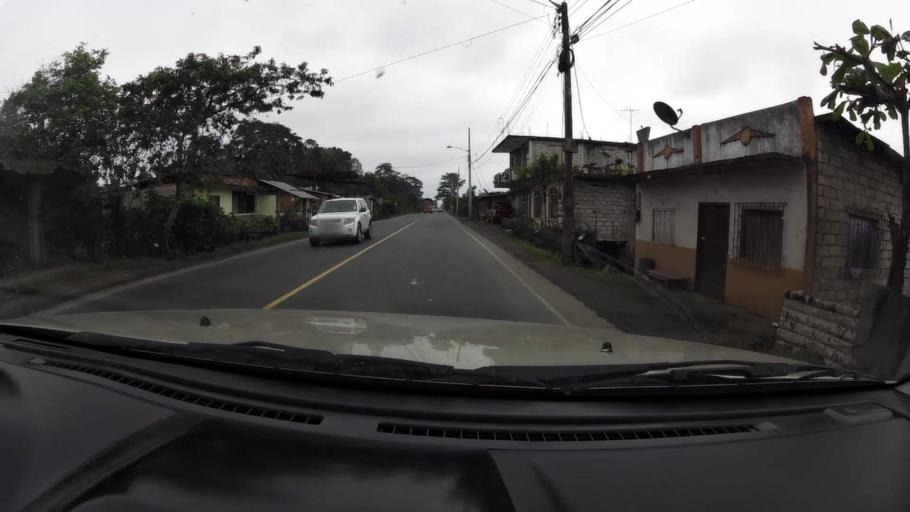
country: EC
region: Guayas
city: Balao
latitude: -3.1083
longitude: -79.7676
